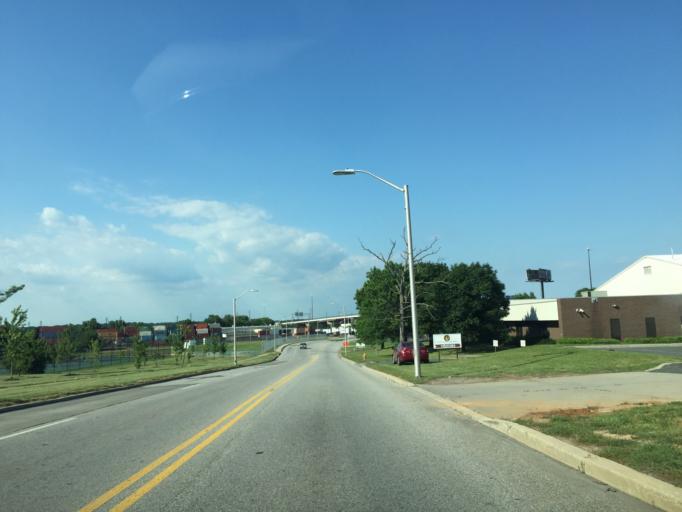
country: US
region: Maryland
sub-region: Baltimore County
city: Rosedale
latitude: 39.2930
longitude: -76.5353
